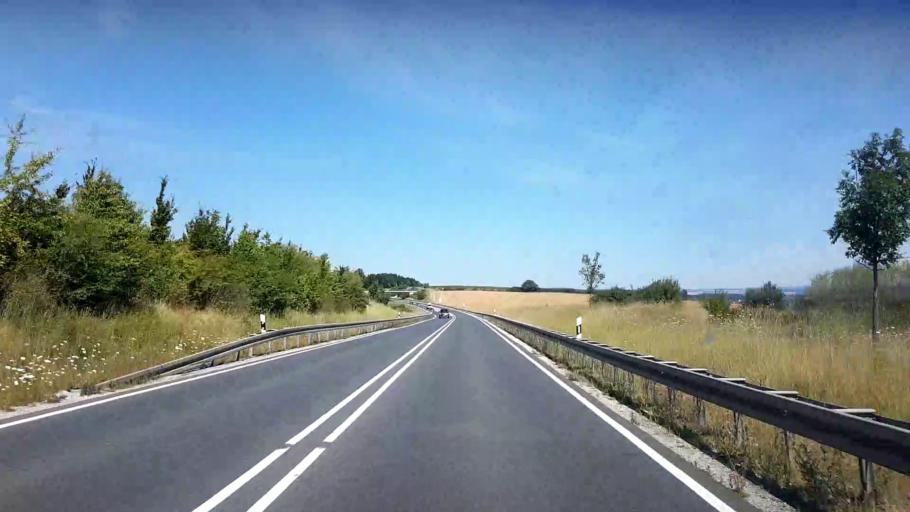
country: DE
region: Bavaria
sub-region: Upper Franconia
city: Untersiemau
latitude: 50.1739
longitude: 10.9878
